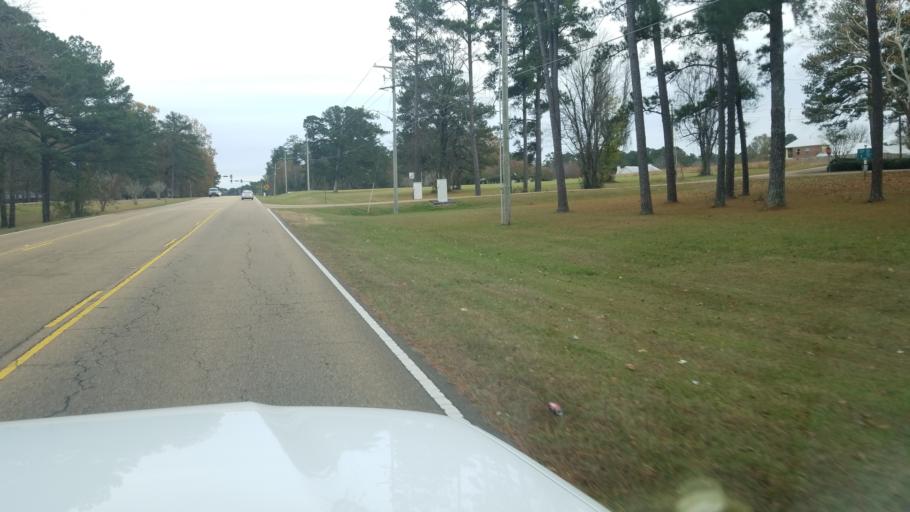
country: US
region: Mississippi
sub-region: Rankin County
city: Brandon
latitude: 32.3760
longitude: -90.0255
